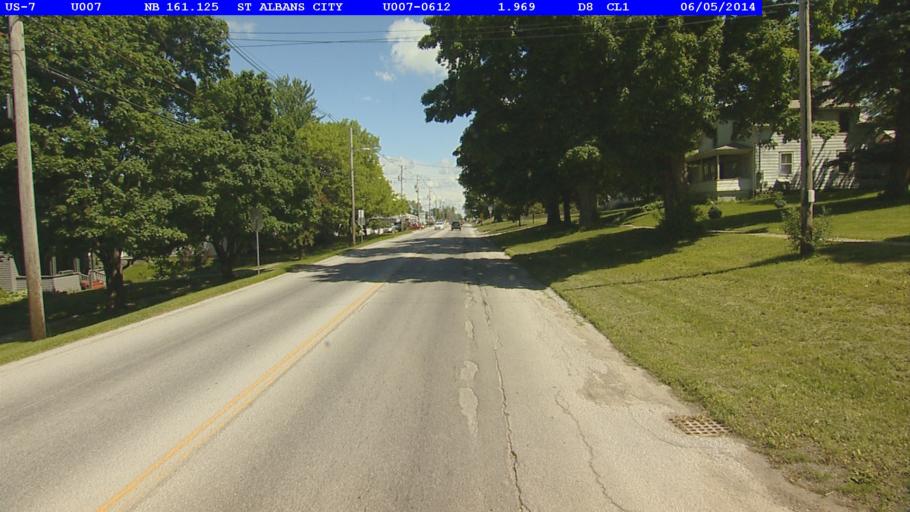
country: US
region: Vermont
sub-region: Franklin County
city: Saint Albans
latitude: 44.8211
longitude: -73.0815
